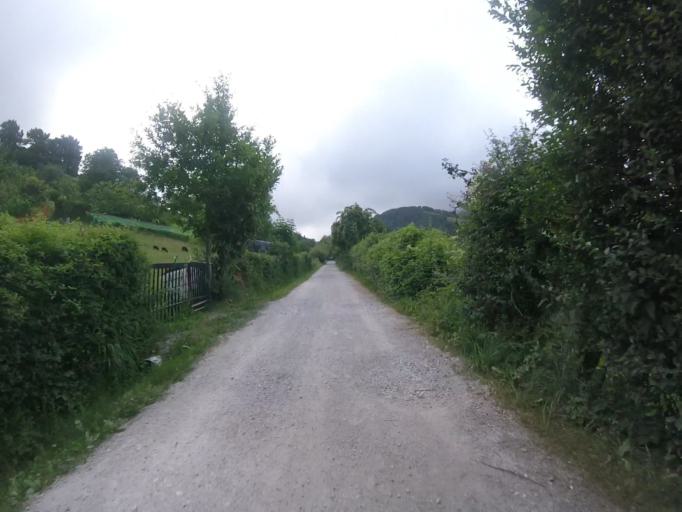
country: ES
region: Navarre
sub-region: Provincia de Navarra
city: Leitza
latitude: 43.0863
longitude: -1.9156
